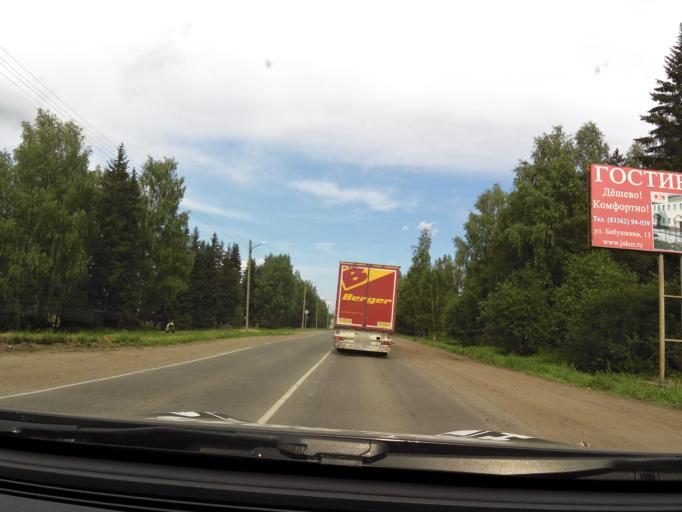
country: RU
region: Kirov
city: Stulovo
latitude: 58.7166
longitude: 50.1293
